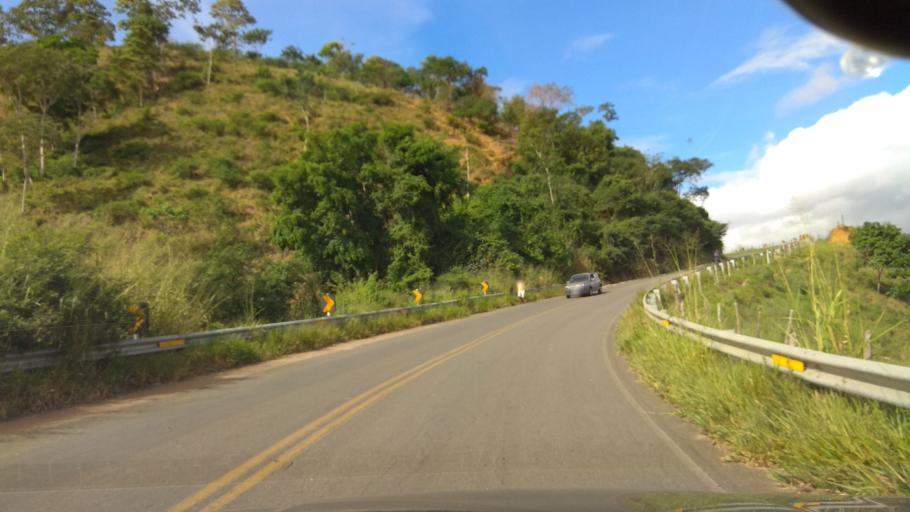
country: BR
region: Bahia
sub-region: Ubaira
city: Ubaira
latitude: -13.2538
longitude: -39.6638
